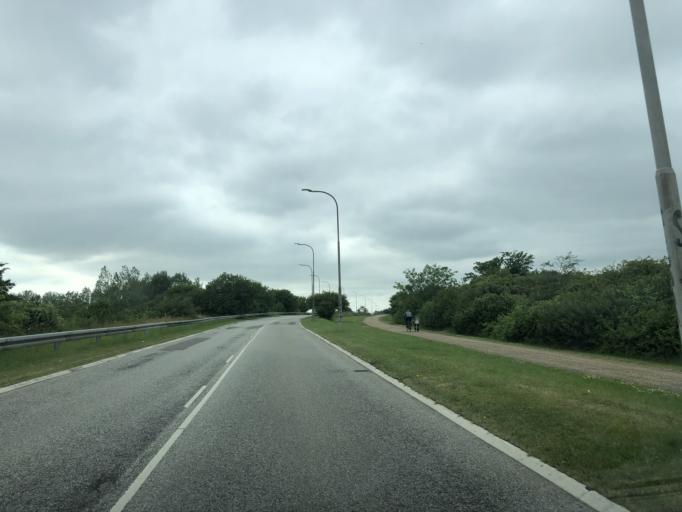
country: DK
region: Capital Region
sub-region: Ishoj Kommune
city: Ishoj
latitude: 55.6020
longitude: 12.3454
